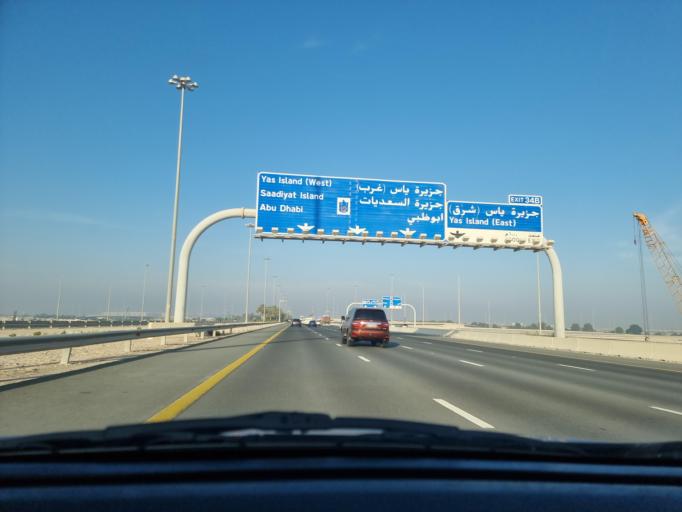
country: AE
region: Abu Dhabi
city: Abu Dhabi
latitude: 24.4827
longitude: 54.6534
